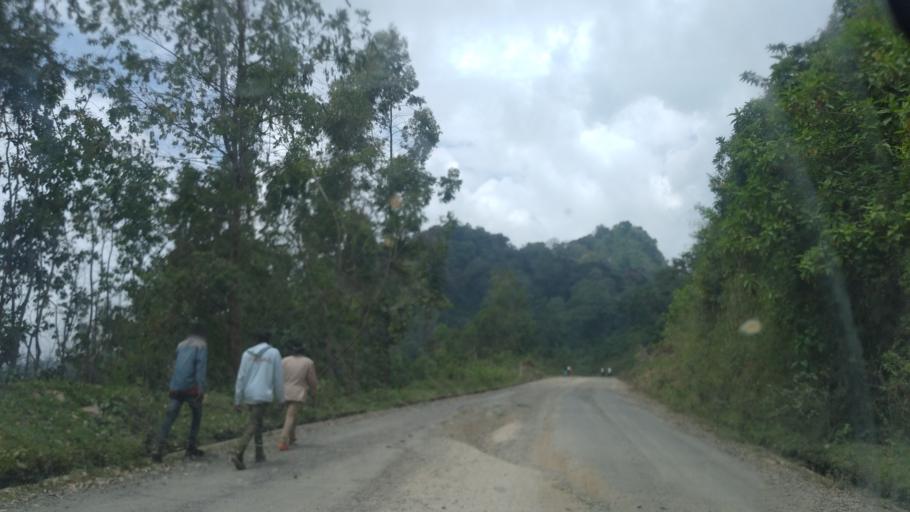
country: ET
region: Southern Nations, Nationalities, and People's Region
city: Bonga
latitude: 7.1132
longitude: 36.7268
